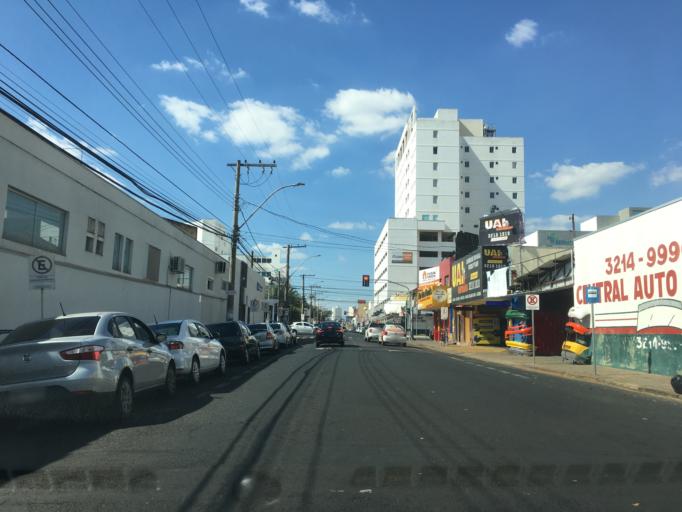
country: BR
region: Minas Gerais
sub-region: Uberlandia
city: Uberlandia
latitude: -18.9149
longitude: -48.2868
